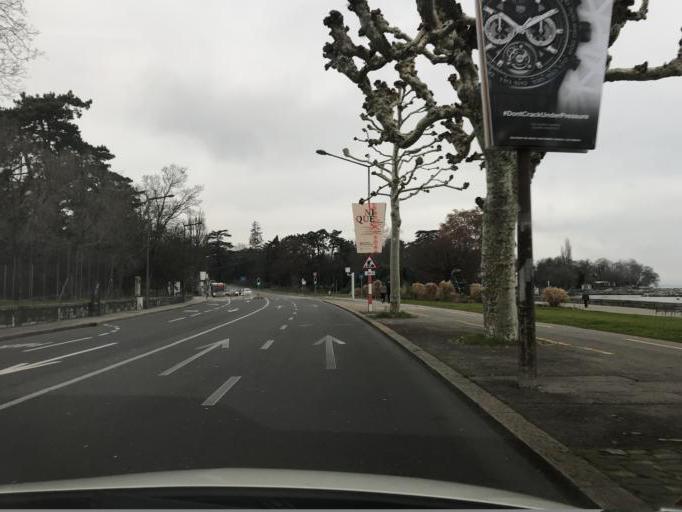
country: CH
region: Geneva
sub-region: Geneva
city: Geneve
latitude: 46.2158
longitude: 6.1517
